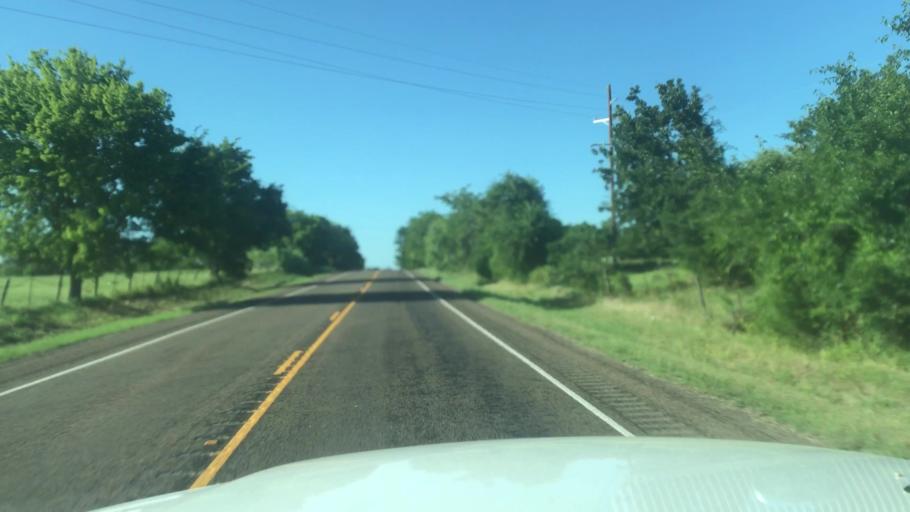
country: US
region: Texas
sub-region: Grimes County
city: Anderson
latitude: 30.6234
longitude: -95.8835
